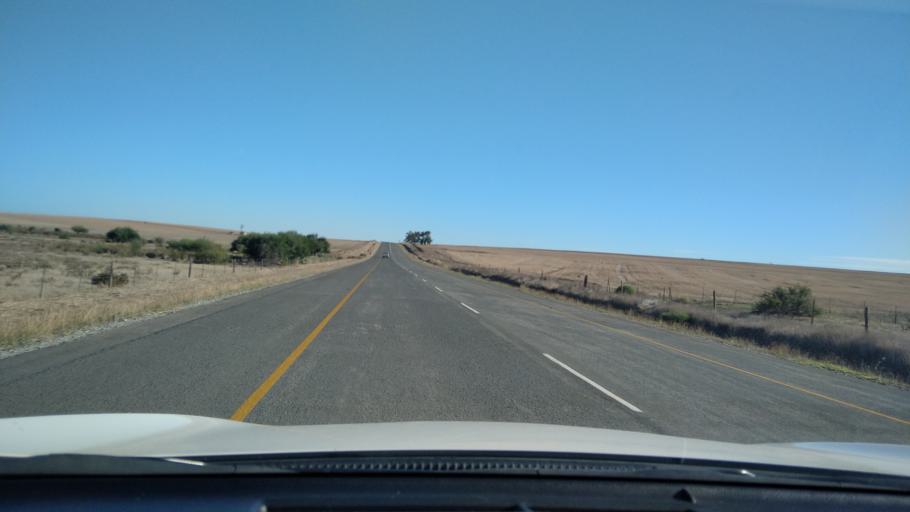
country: ZA
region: Western Cape
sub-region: West Coast District Municipality
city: Malmesbury
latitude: -33.3422
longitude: 18.6369
